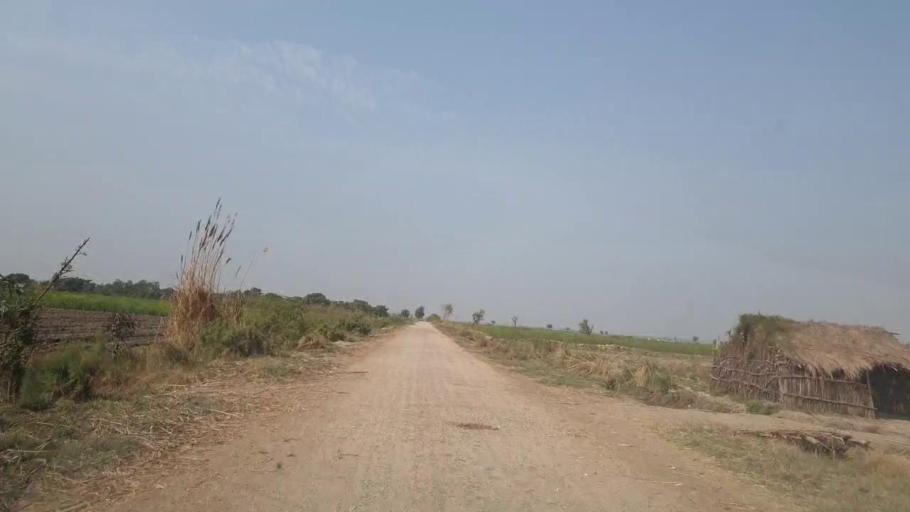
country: PK
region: Sindh
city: Mirpur Khas
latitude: 25.5824
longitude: 69.1369
